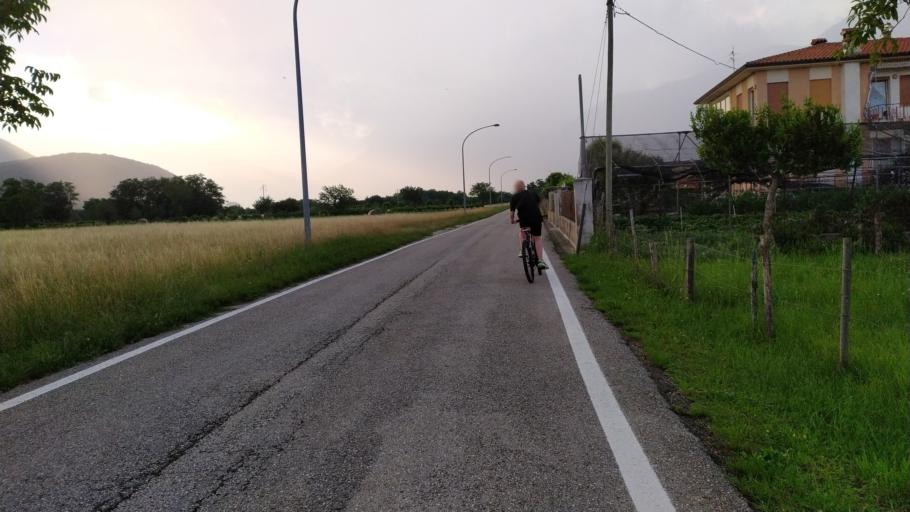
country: IT
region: Veneto
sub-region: Provincia di Vicenza
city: Carre
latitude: 45.7528
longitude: 11.4539
